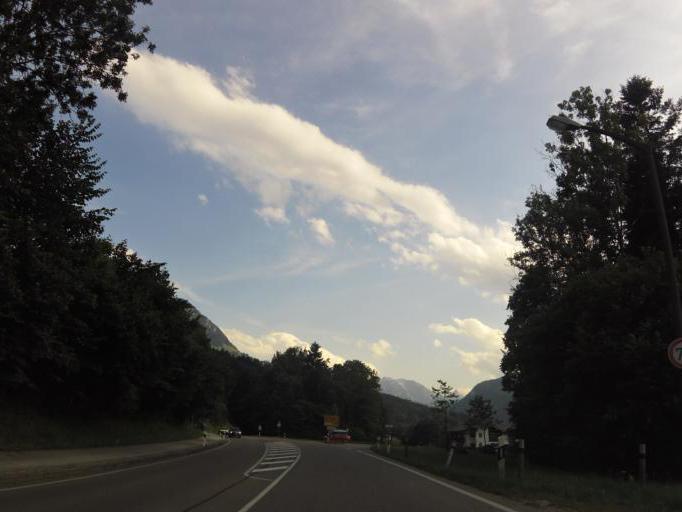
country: DE
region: Bavaria
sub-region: Upper Bavaria
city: Berchtesgaden
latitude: 47.6187
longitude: 12.9996
